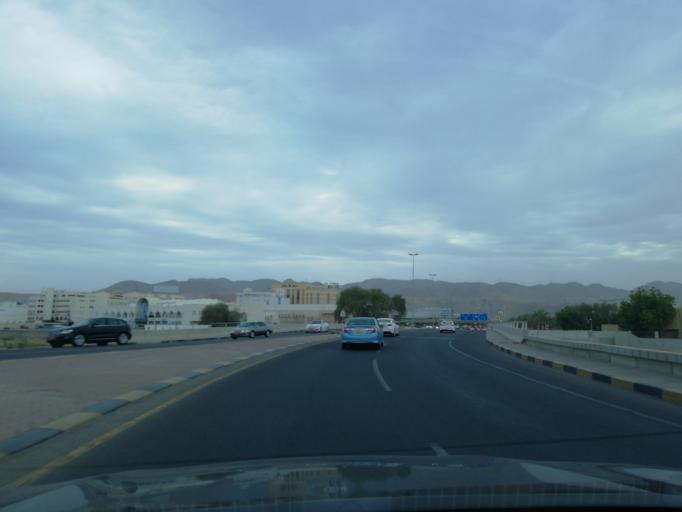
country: OM
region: Muhafazat Masqat
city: Muscat
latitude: 23.6159
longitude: 58.4943
